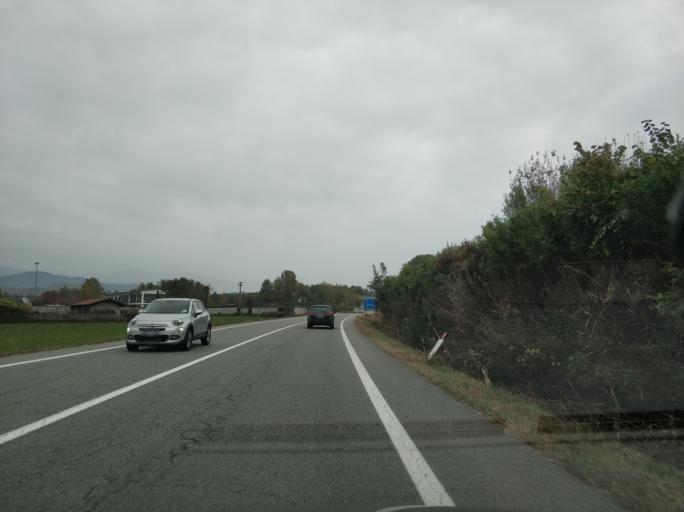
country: IT
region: Piedmont
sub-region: Provincia di Torino
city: Bairo
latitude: 45.3834
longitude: 7.7345
